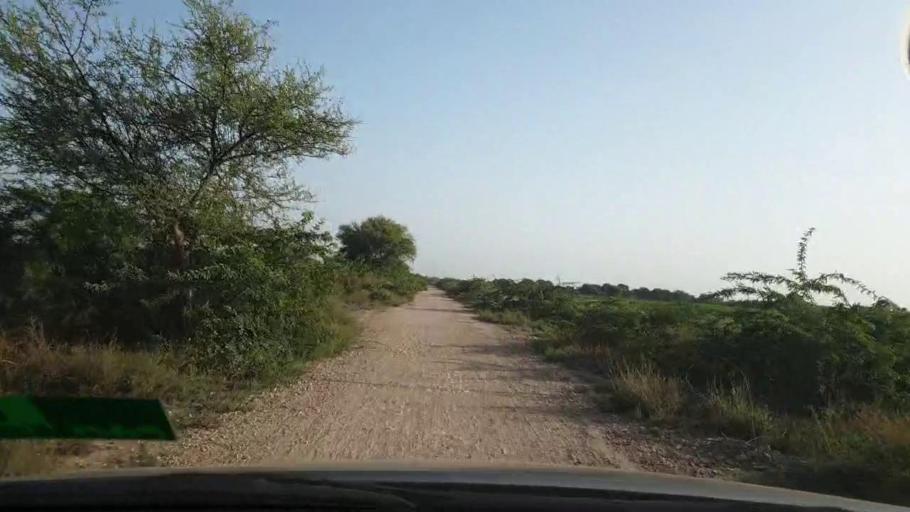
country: PK
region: Sindh
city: Naukot
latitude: 24.7284
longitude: 69.2258
